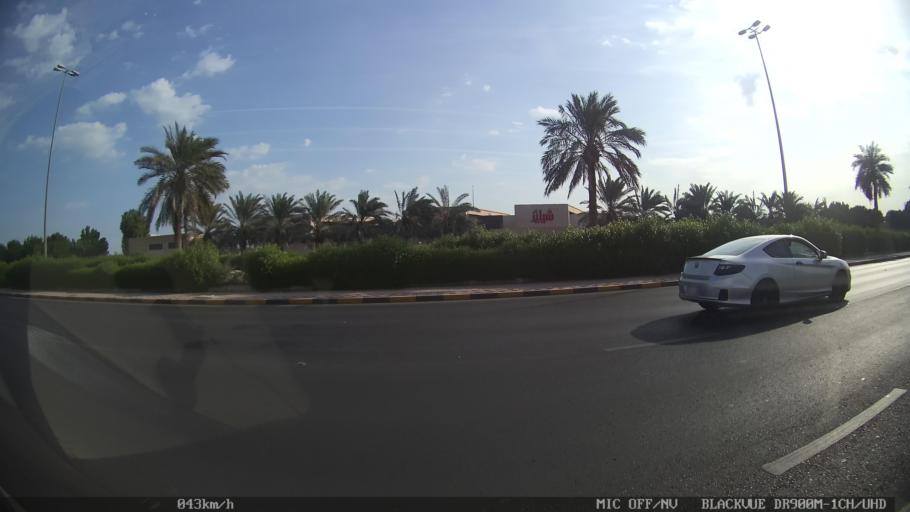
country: KW
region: Al Asimah
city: Ad Dasmah
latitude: 29.3635
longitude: 48.0231
